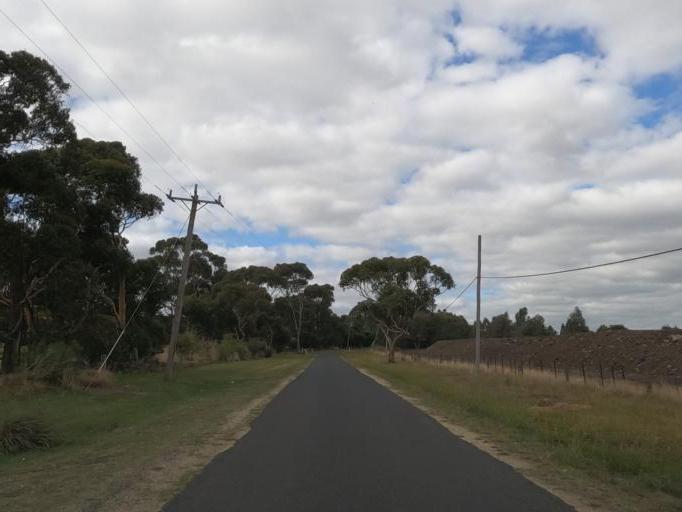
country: AU
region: Victoria
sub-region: Hume
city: Greenvale
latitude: -37.5610
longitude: 144.8657
